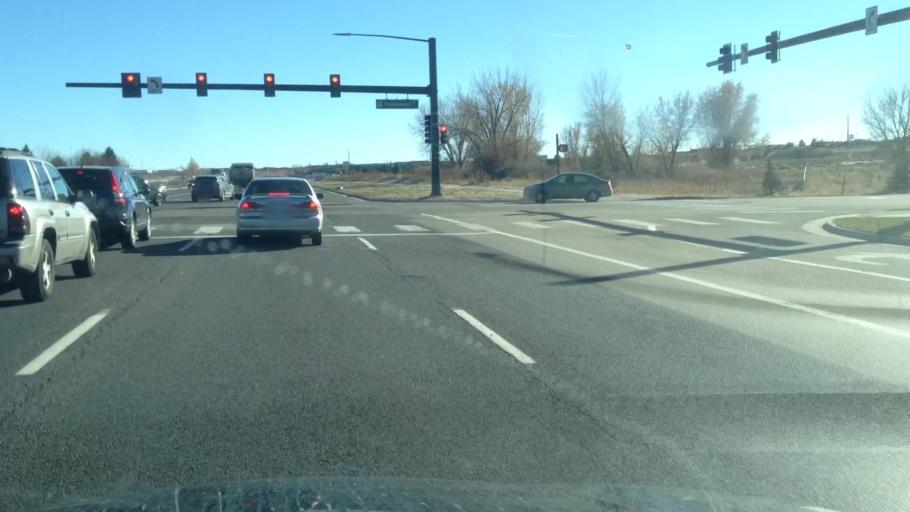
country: US
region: Colorado
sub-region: Douglas County
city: Stonegate
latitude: 39.5546
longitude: -104.7947
